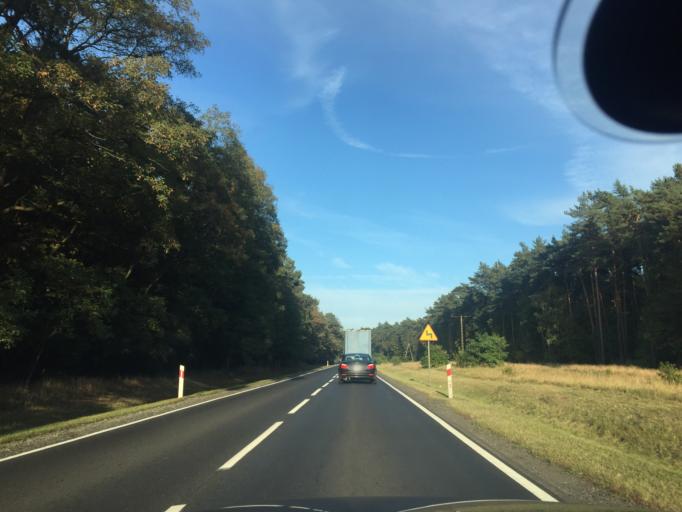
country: PL
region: Kujawsko-Pomorskie
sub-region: Powiat torunski
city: Wielka Nieszawka
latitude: 52.9164
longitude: 18.4923
